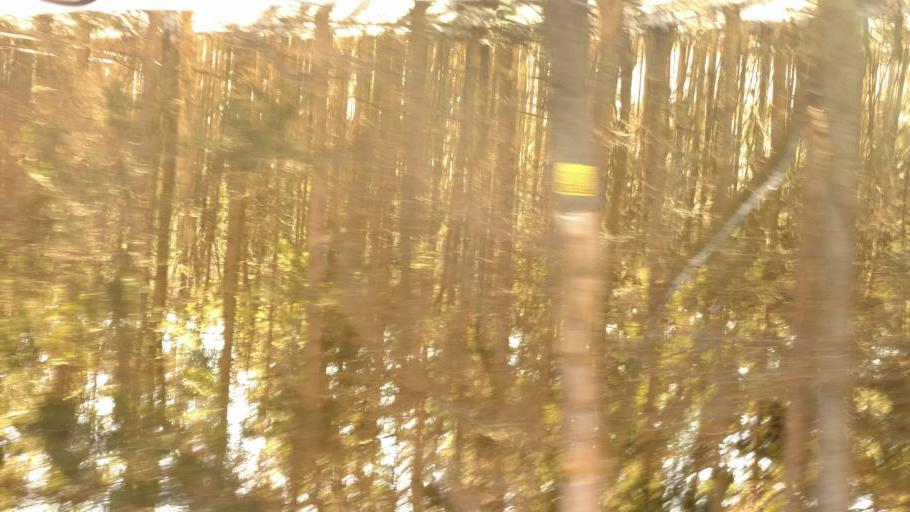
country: US
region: New York
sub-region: Allegany County
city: Wellsville
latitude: 42.0669
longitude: -78.0109
